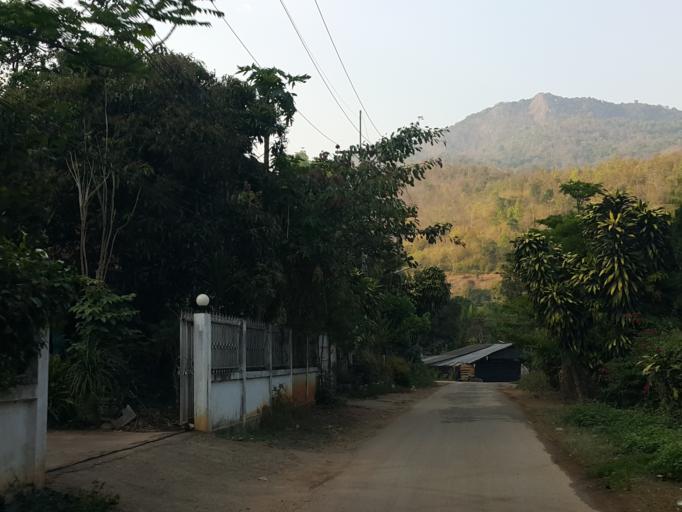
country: TH
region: Chiang Mai
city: Samoeng
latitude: 18.8954
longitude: 98.8323
